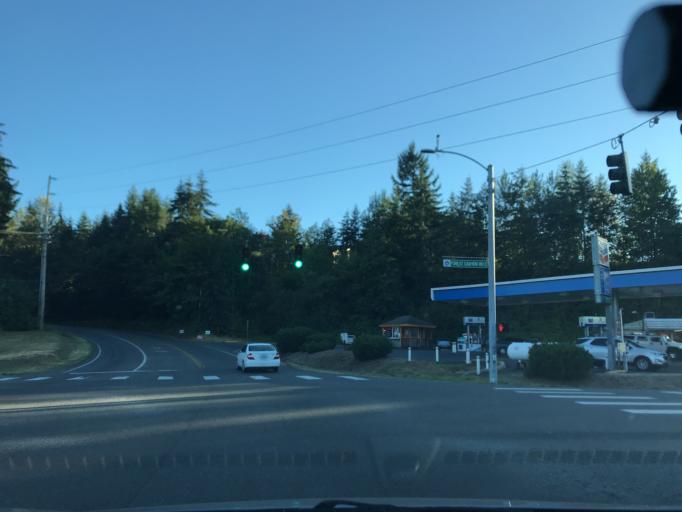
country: US
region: Washington
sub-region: Pierce County
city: Sumner
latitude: 47.2285
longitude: -122.2013
